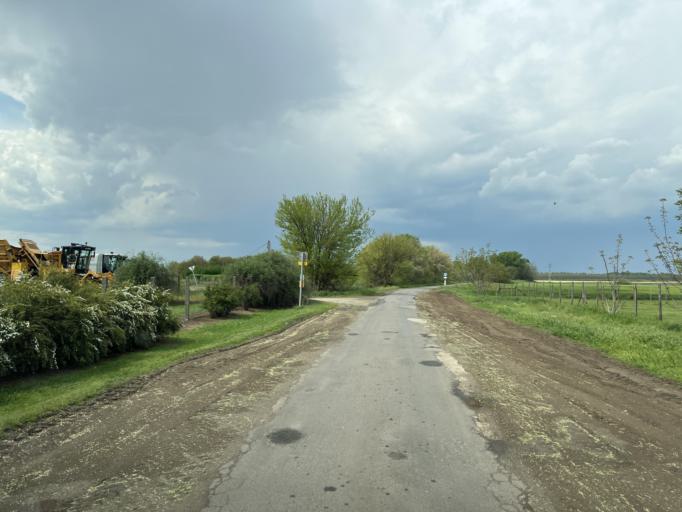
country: HU
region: Pest
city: Nagykoros
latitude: 46.9826
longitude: 19.8065
